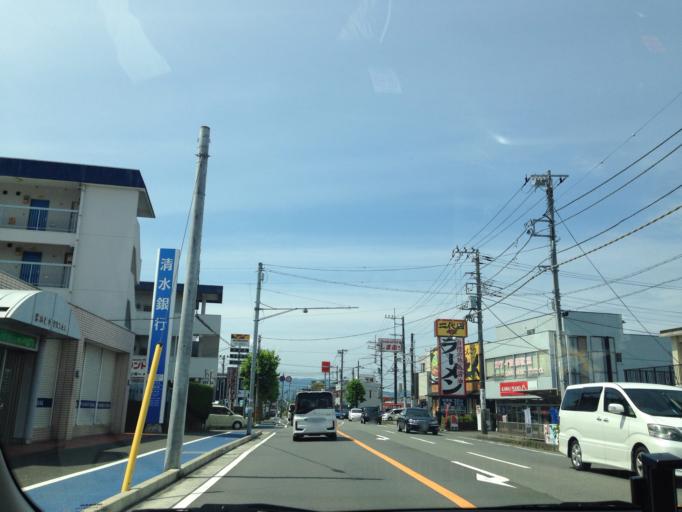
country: JP
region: Shizuoka
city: Numazu
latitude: 35.1207
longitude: 138.8679
